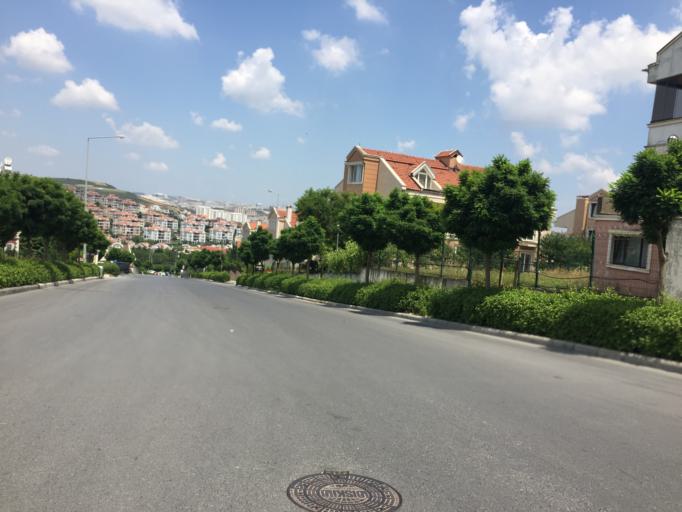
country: TR
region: Istanbul
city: Esenyurt
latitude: 41.0789
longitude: 28.6677
